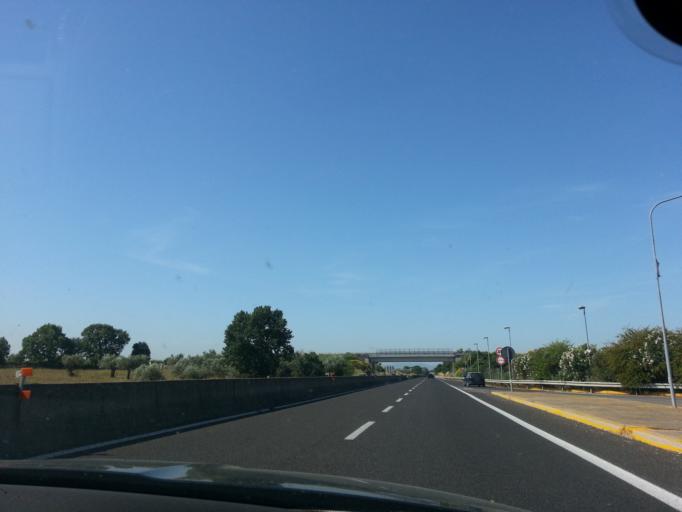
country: IT
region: Latium
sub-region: Provincia di Viterbo
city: Viterbo
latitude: 42.4127
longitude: 12.0746
